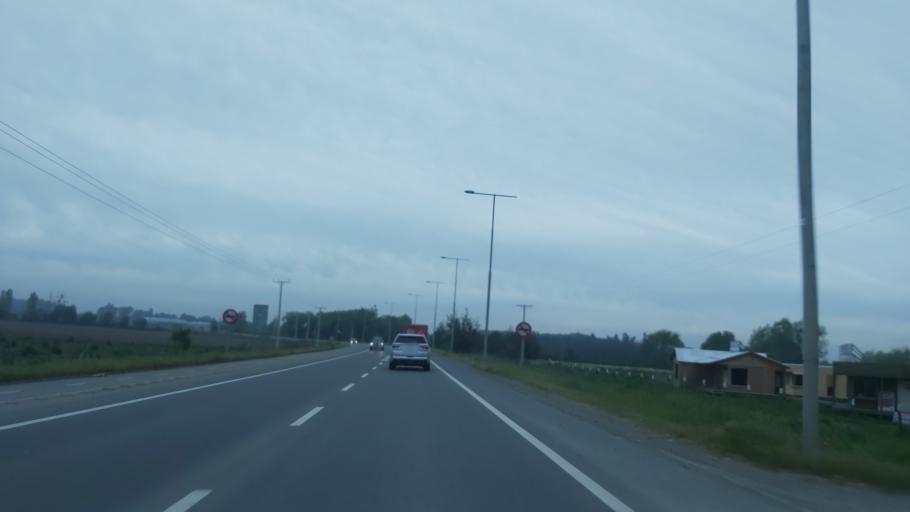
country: CL
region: Maule
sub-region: Provincia de Linares
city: Linares
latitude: -35.8309
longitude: -71.6160
